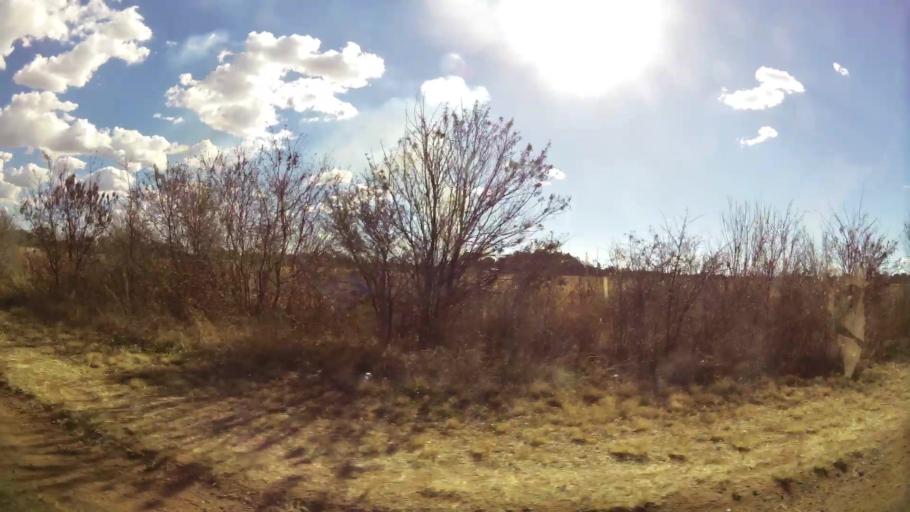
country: ZA
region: North-West
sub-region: Dr Kenneth Kaunda District Municipality
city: Klerksdorp
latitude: -26.8492
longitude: 26.6507
